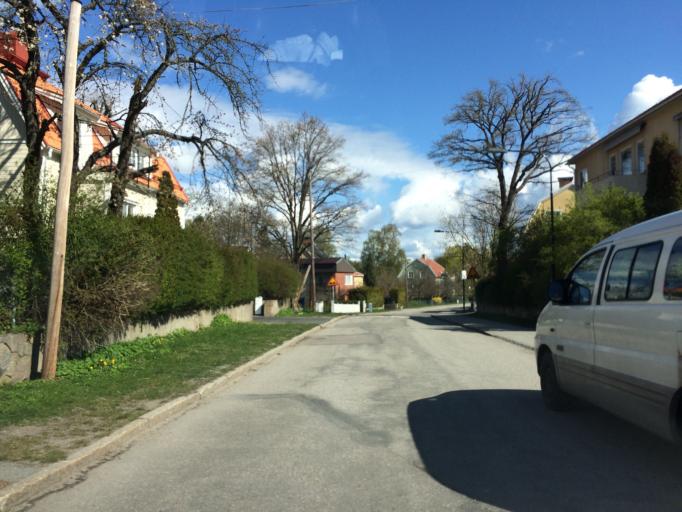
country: SE
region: Stockholm
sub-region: Huddinge Kommun
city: Segeltorp
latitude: 59.2985
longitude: 17.9490
